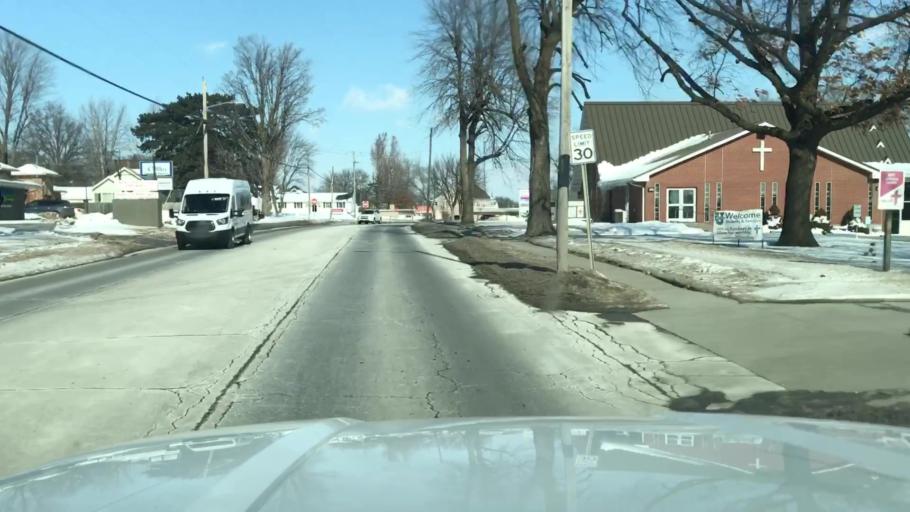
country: US
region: Missouri
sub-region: Nodaway County
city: Maryville
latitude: 40.3369
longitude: -94.8738
